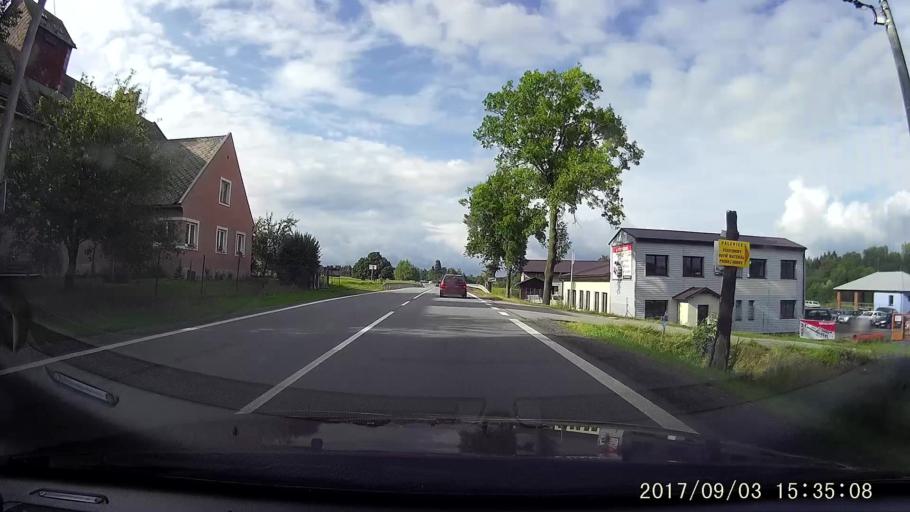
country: CZ
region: Vysocina
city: Knezice
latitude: 49.2866
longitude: 15.5830
